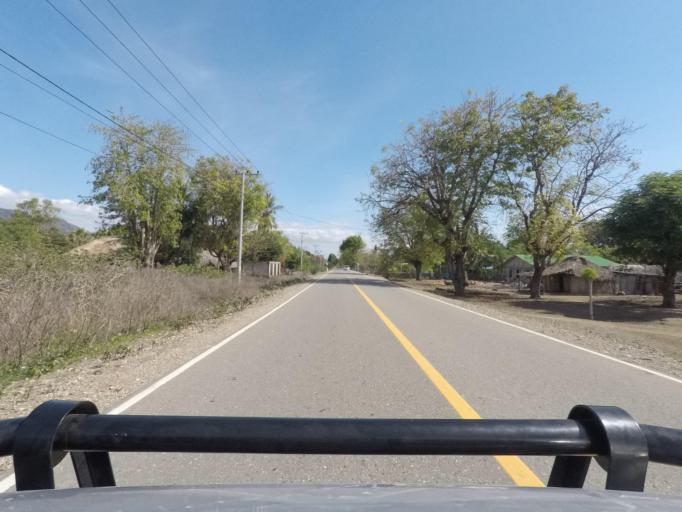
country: ID
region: East Nusa Tenggara
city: Atambua
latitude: -8.8962
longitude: 125.0025
